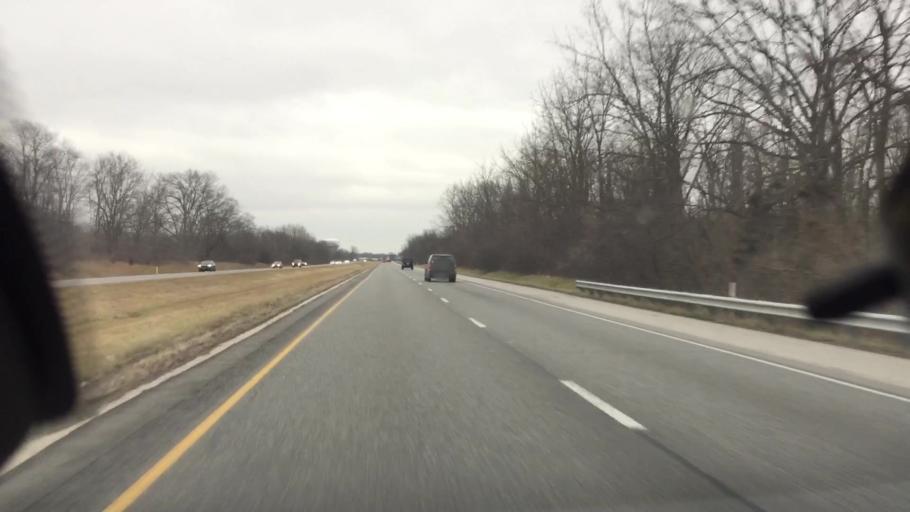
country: US
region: Indiana
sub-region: Hendricks County
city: Pittsboro
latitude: 39.8735
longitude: -86.4270
